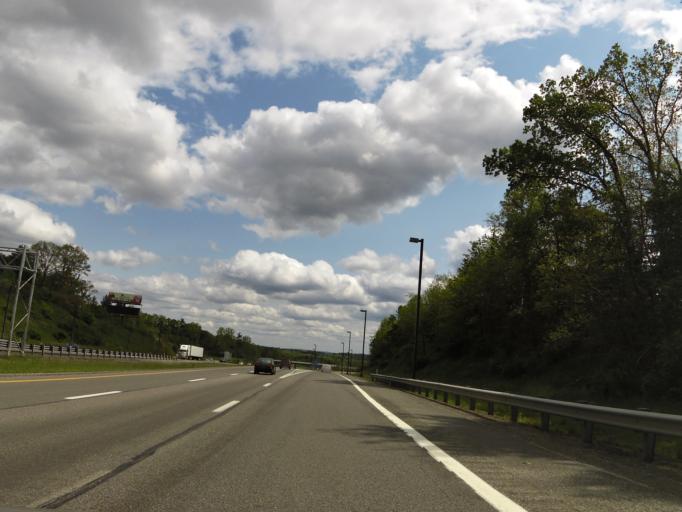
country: US
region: West Virginia
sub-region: Raleigh County
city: Prosperity
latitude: 37.8149
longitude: -81.2149
